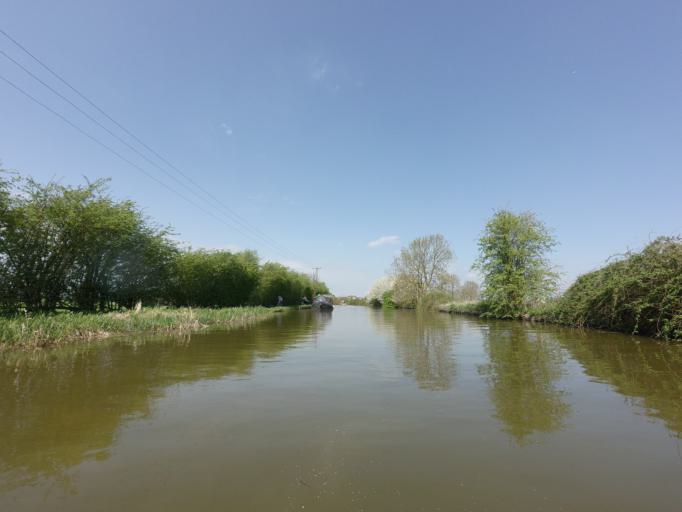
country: GB
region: England
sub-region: Buckinghamshire
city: Cheddington
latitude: 51.8684
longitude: -0.6486
